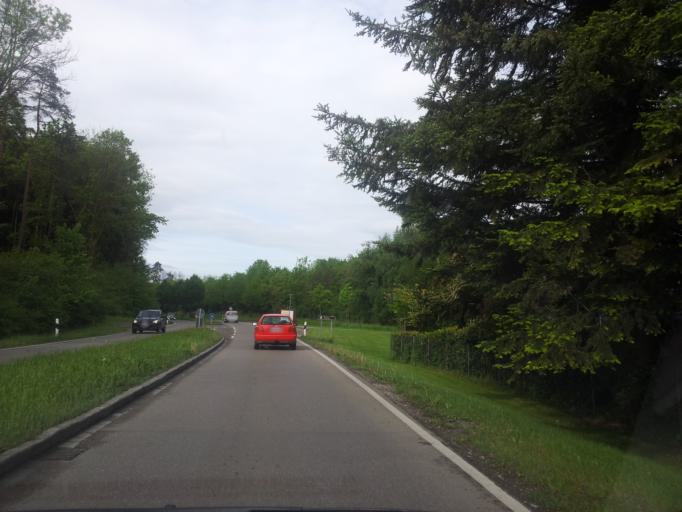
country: DE
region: Bavaria
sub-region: Swabia
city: Weissensberg
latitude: 47.5754
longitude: 9.7090
